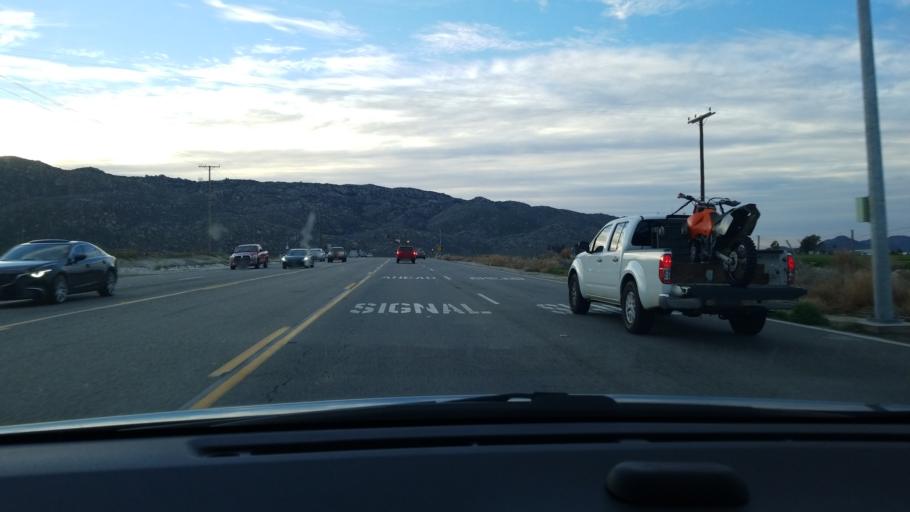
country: US
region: California
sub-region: Riverside County
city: San Jacinto
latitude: 33.8235
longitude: -117.0310
